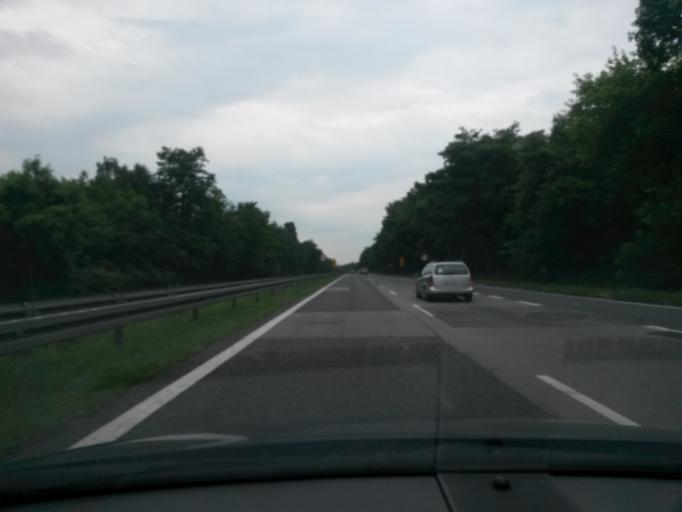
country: PL
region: Silesian Voivodeship
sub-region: Czestochowa
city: Czestochowa
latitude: 50.8445
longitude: 19.1493
